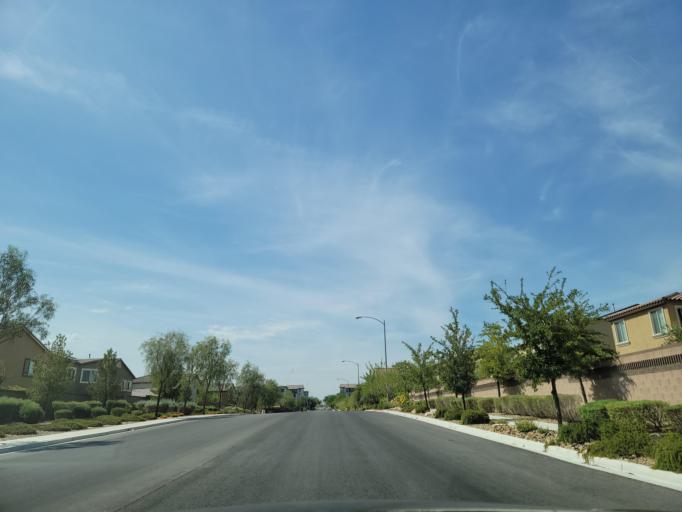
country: US
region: Nevada
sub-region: Clark County
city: Spring Valley
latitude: 36.0773
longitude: -115.2840
